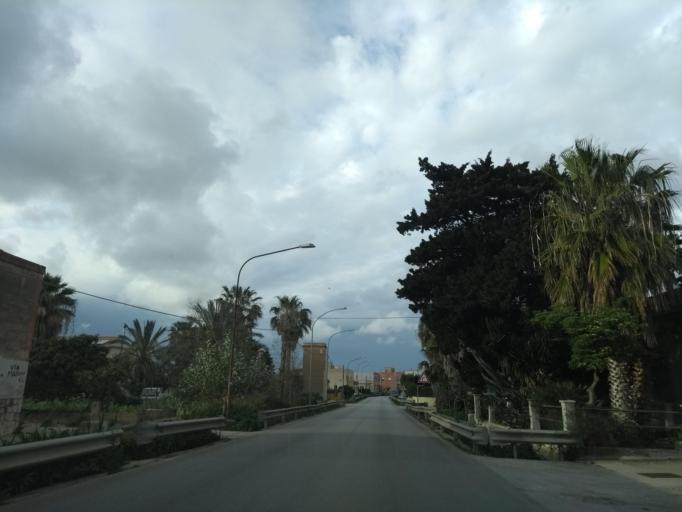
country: IT
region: Sicily
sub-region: Trapani
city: Marausa
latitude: 37.9634
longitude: 12.5183
